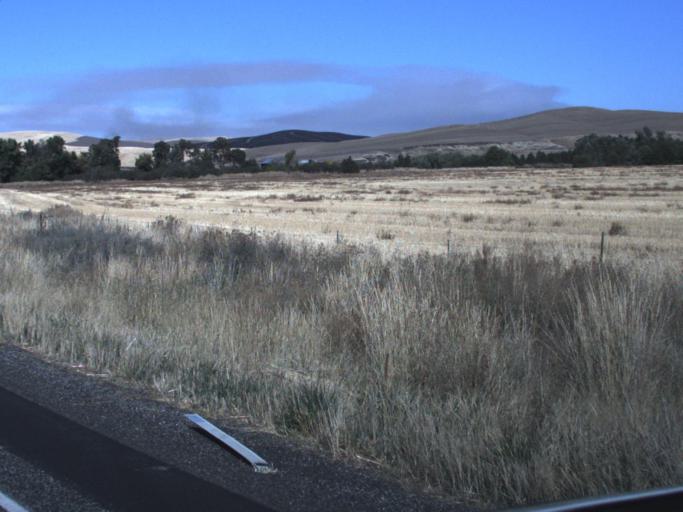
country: US
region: Washington
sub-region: Walla Walla County
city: Waitsburg
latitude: 46.2691
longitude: -118.2210
